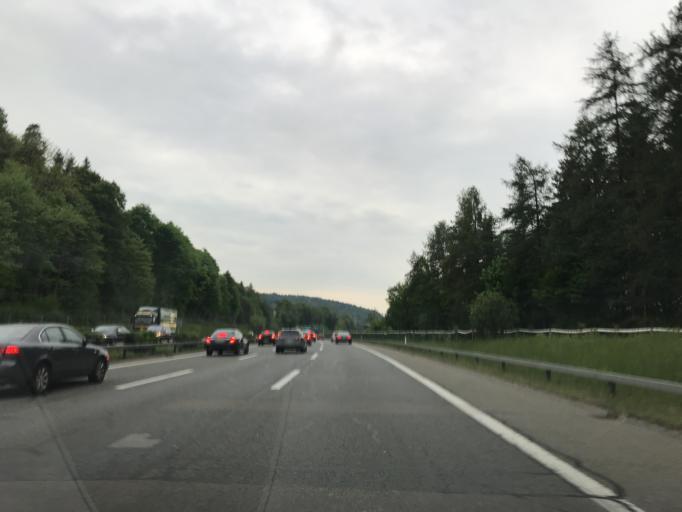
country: CH
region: Zurich
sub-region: Bezirk Winterthur
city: Toss
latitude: 47.4678
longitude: 8.7073
